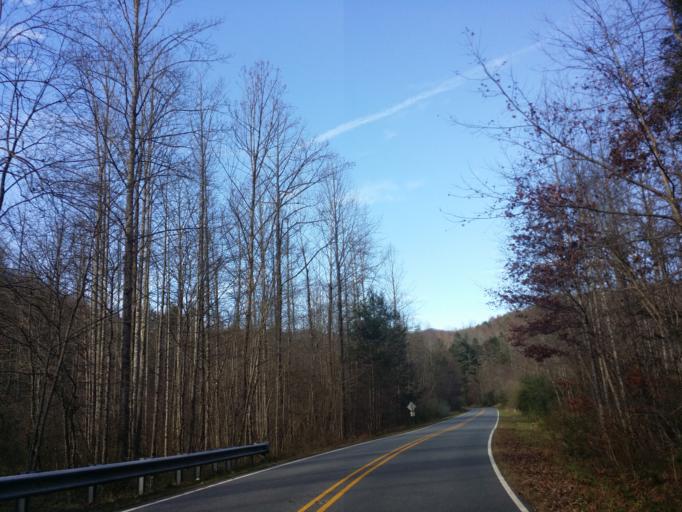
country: US
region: North Carolina
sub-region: McDowell County
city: West Marion
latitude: 35.7372
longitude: -82.1356
